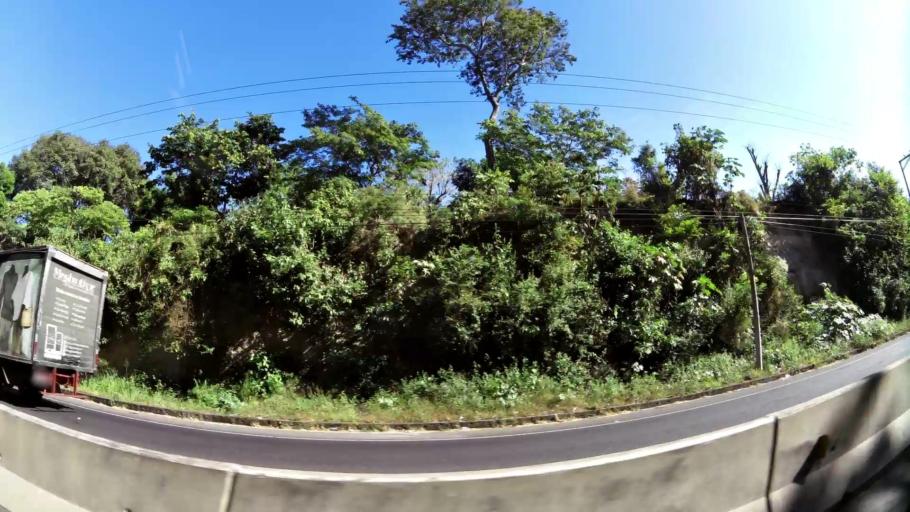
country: SV
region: Santa Ana
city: Coatepeque
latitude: 13.9392
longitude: -89.5426
